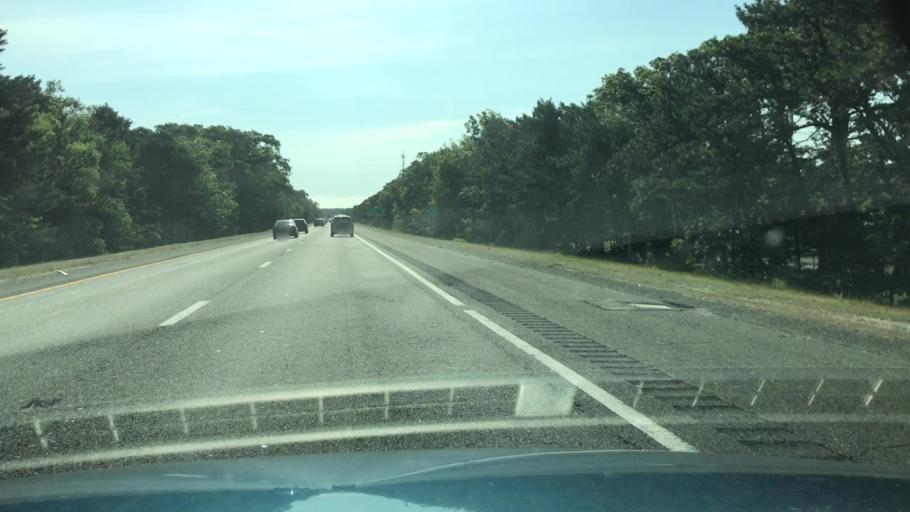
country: US
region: Massachusetts
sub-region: Barnstable County
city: Yarmouth
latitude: 41.6906
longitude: -70.2037
